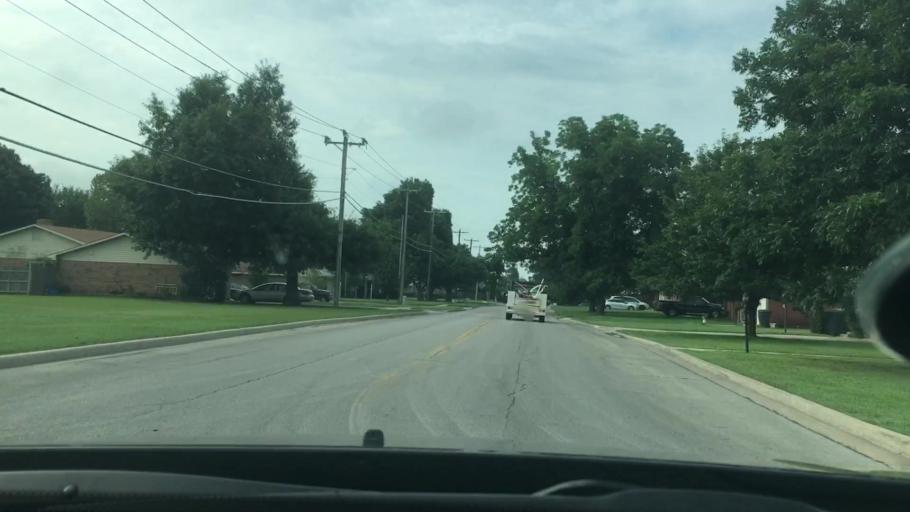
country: US
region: Oklahoma
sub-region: Carter County
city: Ardmore
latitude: 34.1947
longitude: -97.1255
